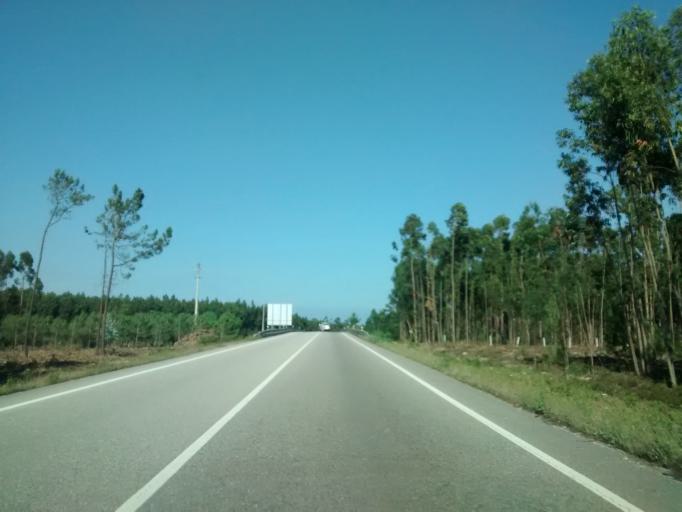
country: PT
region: Leiria
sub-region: Pombal
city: Lourical
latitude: 39.9923
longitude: -8.7998
